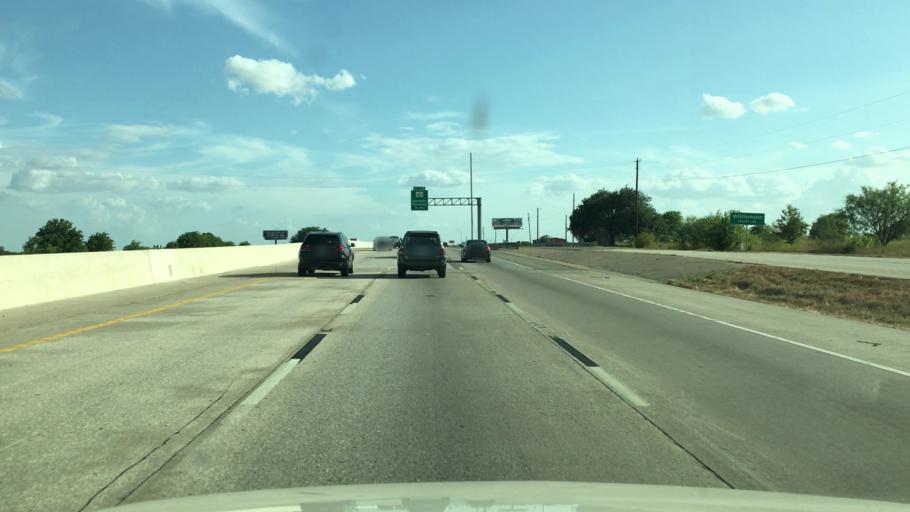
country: US
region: Texas
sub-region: Bell County
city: Salado
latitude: 30.8571
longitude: -97.5894
